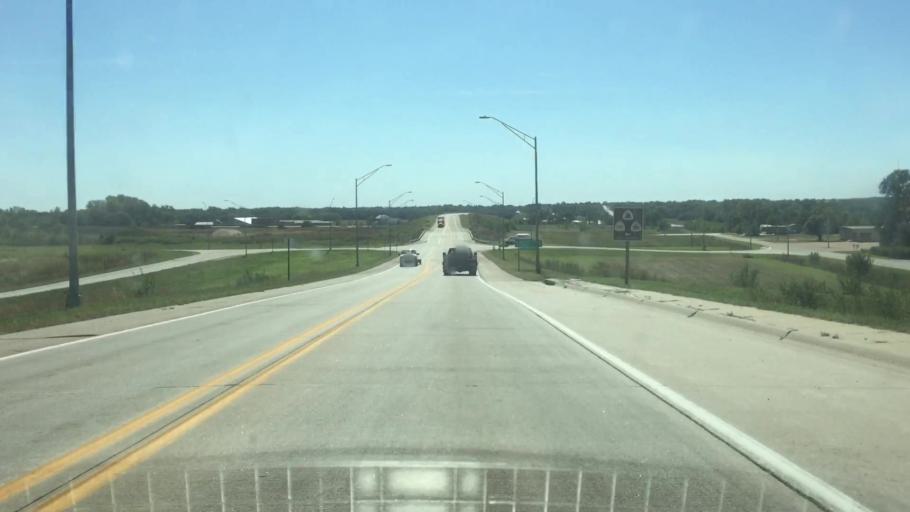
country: US
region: Nebraska
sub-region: Jefferson County
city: Fairbury
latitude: 40.1308
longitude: -97.1705
